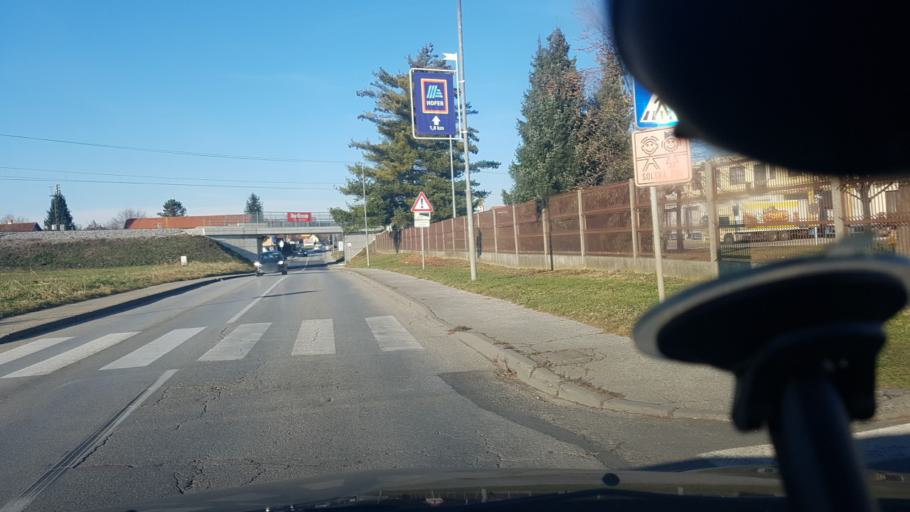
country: SI
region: Ptuj
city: Ptuj
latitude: 46.4100
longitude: 15.8656
